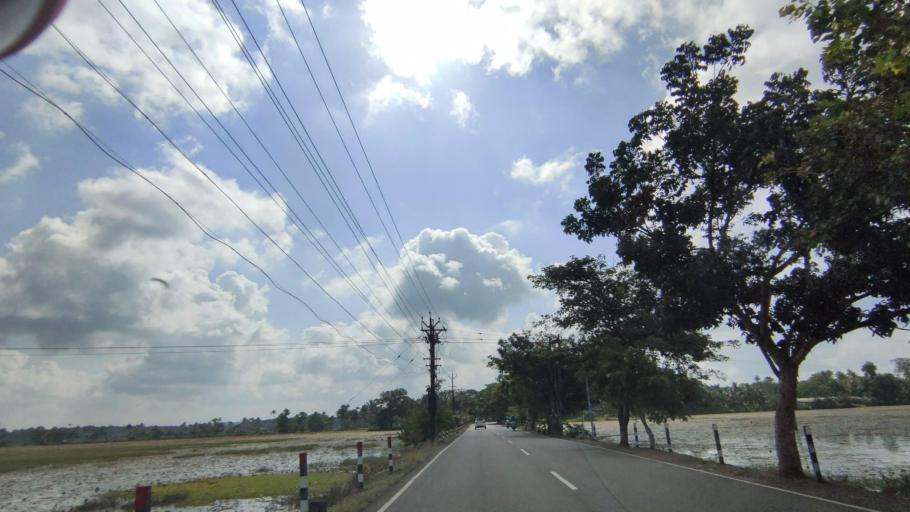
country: IN
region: Kerala
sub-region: Kottayam
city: Kottayam
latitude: 9.6915
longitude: 76.4947
